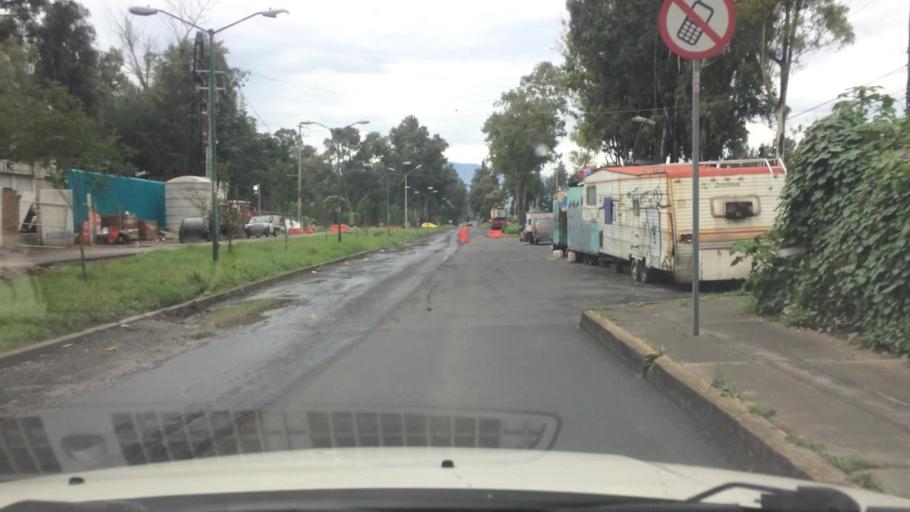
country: MX
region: Mexico City
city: Iztapalapa
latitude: 19.3186
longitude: -99.0996
